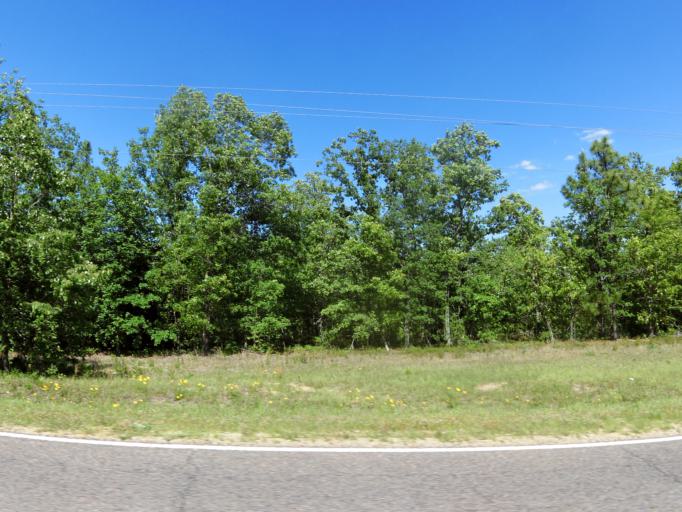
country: US
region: South Carolina
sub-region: Barnwell County
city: Williston
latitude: 33.4522
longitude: -81.4930
